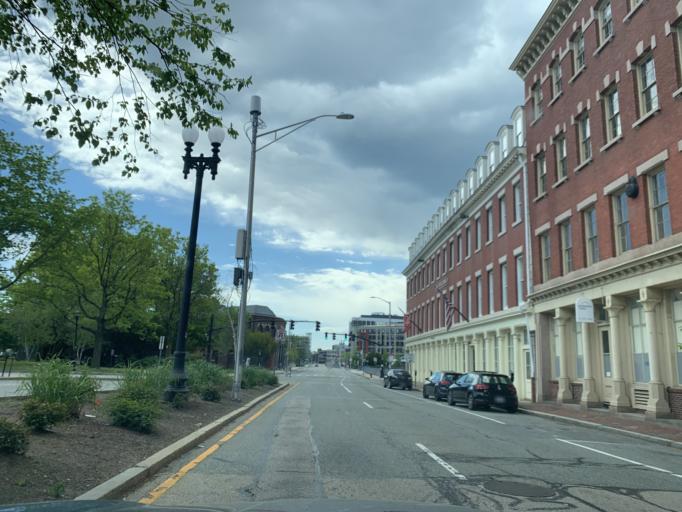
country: US
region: Rhode Island
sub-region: Providence County
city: Providence
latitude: 41.8237
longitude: -71.4083
